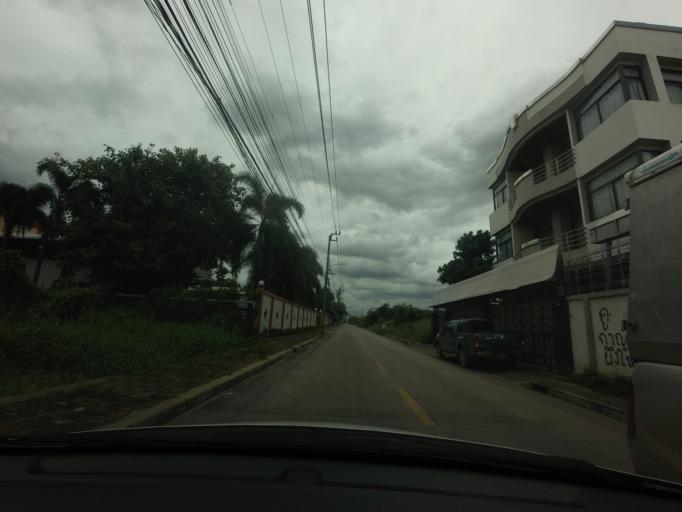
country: TH
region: Bangkok
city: Min Buri
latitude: 13.7922
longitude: 100.7482
